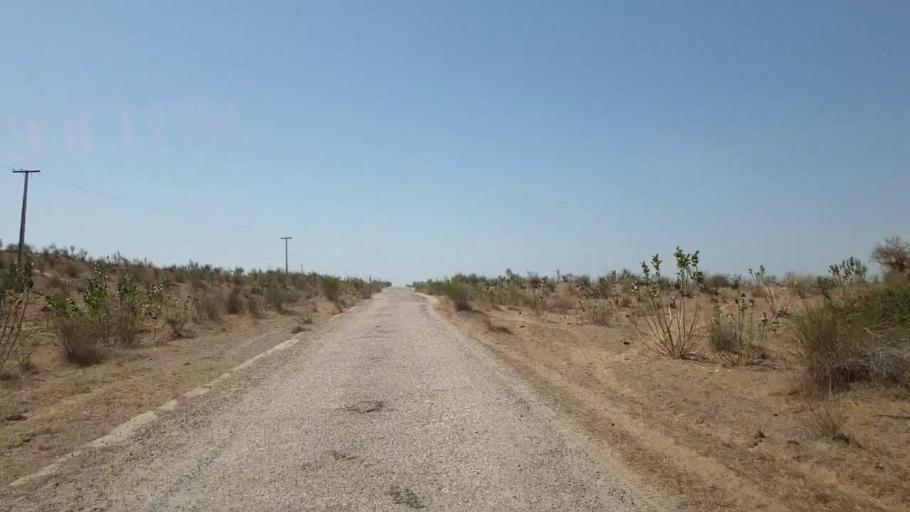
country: PK
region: Sindh
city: Umarkot
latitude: 25.1415
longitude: 69.9260
